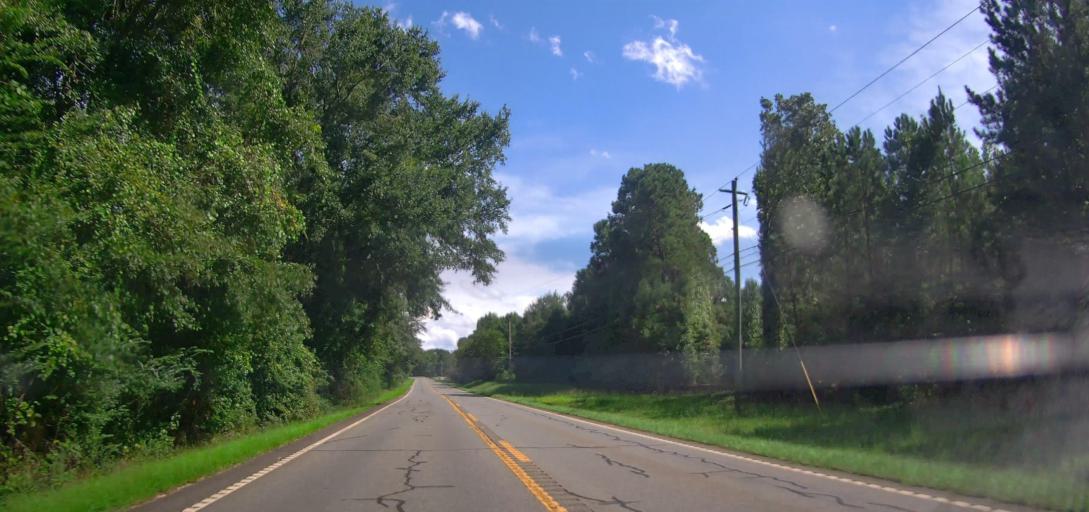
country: US
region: Georgia
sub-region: Talbot County
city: Sardis
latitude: 32.8044
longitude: -84.5919
